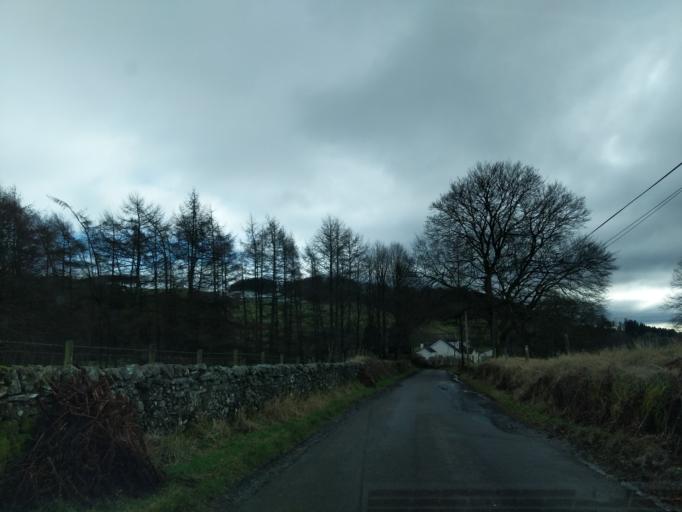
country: GB
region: Scotland
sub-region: Dumfries and Galloway
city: Moffat
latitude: 55.3178
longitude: -3.4230
